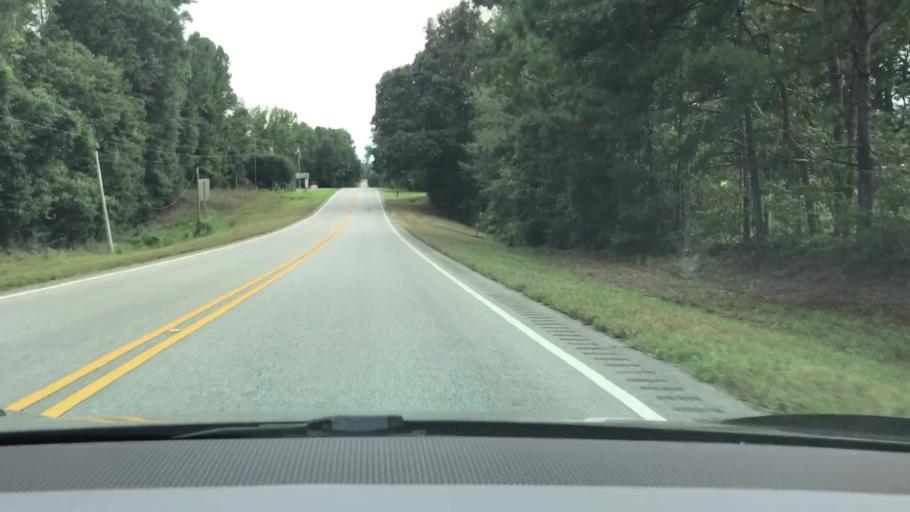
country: US
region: Alabama
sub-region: Pike County
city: Troy
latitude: 31.6268
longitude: -85.9765
